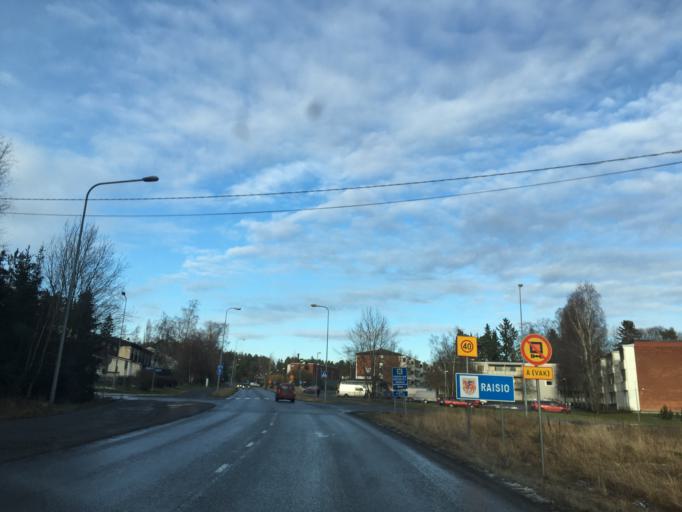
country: FI
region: Varsinais-Suomi
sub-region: Turku
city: Raisio
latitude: 60.4639
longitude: 22.1540
